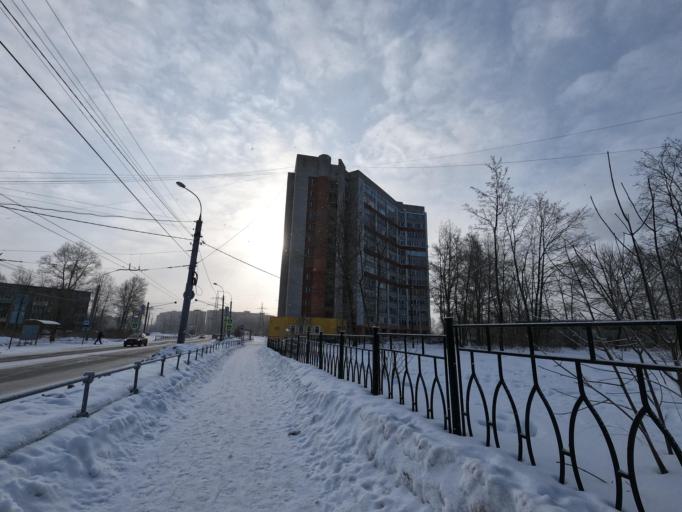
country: RU
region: Jaroslavl
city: Rybinsk
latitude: 58.0502
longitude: 38.7646
